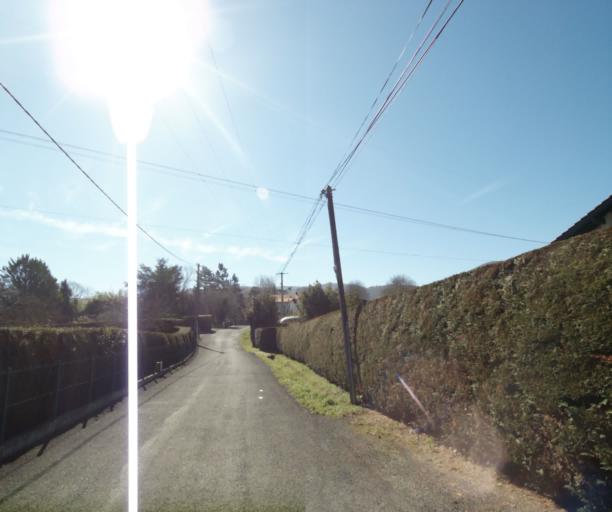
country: FR
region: Aquitaine
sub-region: Departement des Pyrenees-Atlantiques
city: Urrugne
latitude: 43.3438
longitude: -1.6934
